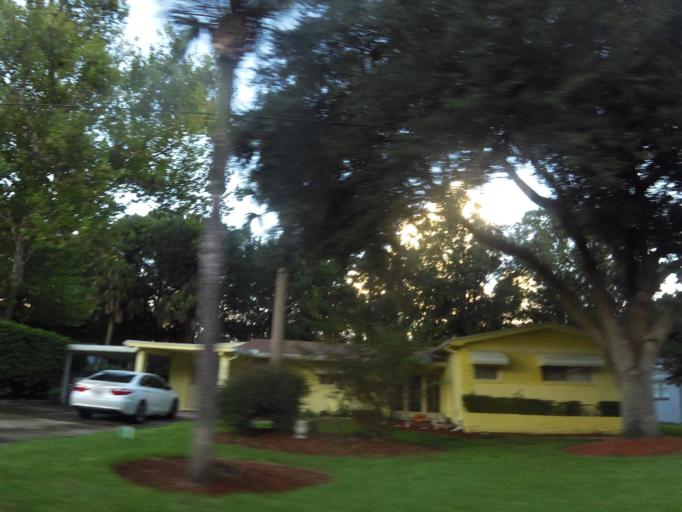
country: US
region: Florida
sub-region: Duval County
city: Jacksonville
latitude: 30.2331
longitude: -81.6140
